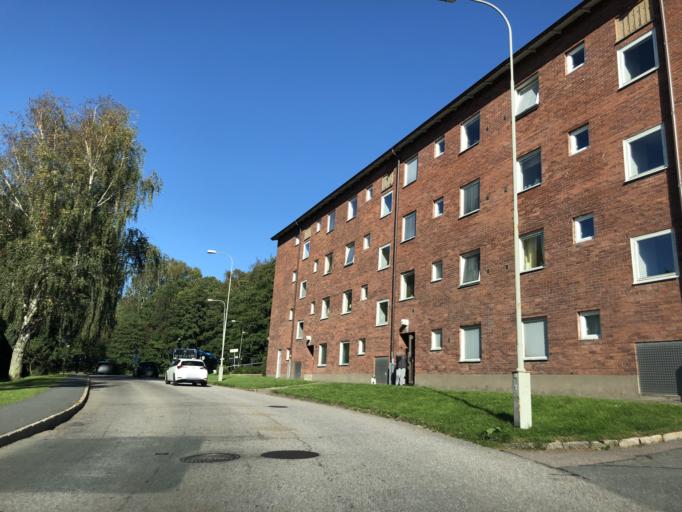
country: SE
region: Vaestra Goetaland
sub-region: Molndal
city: Moelndal
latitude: 57.6800
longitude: 12.0166
